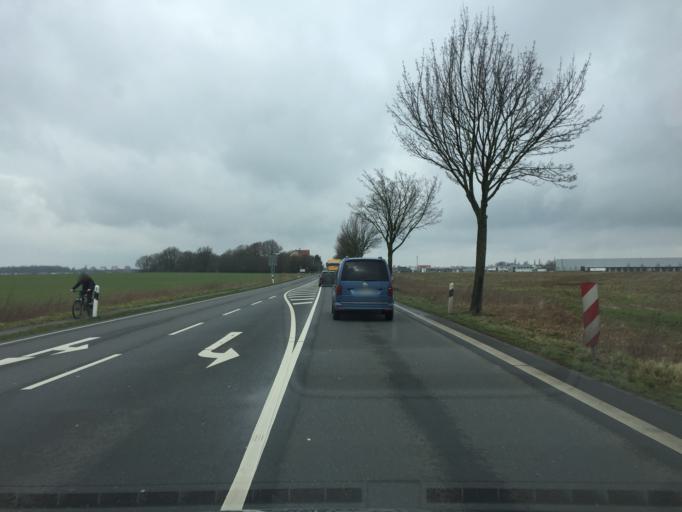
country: DE
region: Lower Saxony
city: Wunstorf
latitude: 52.4036
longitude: 9.4607
